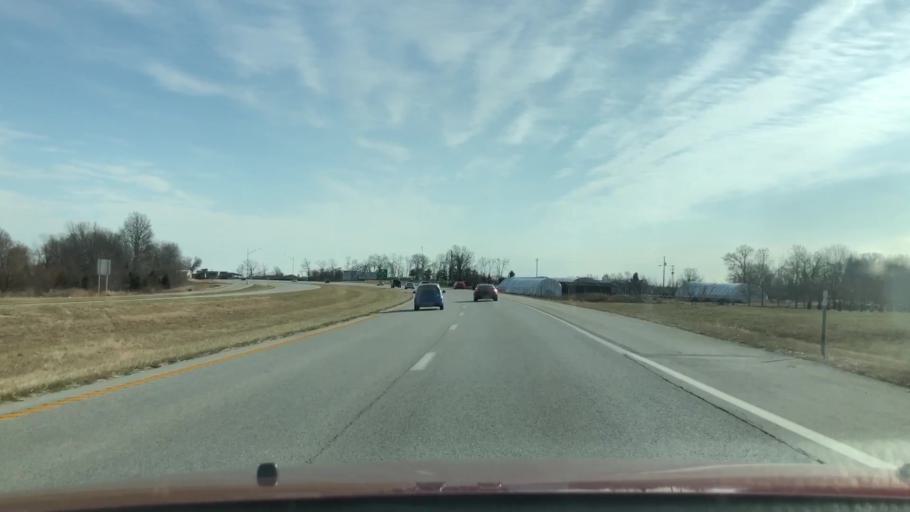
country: US
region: Missouri
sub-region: Webster County
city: Rogersville
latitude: 37.1104
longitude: -93.0677
